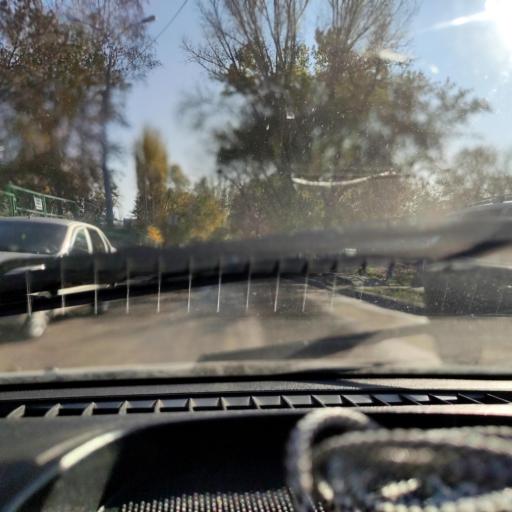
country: RU
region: Samara
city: Tol'yatti
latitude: 53.5278
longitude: 49.4006
